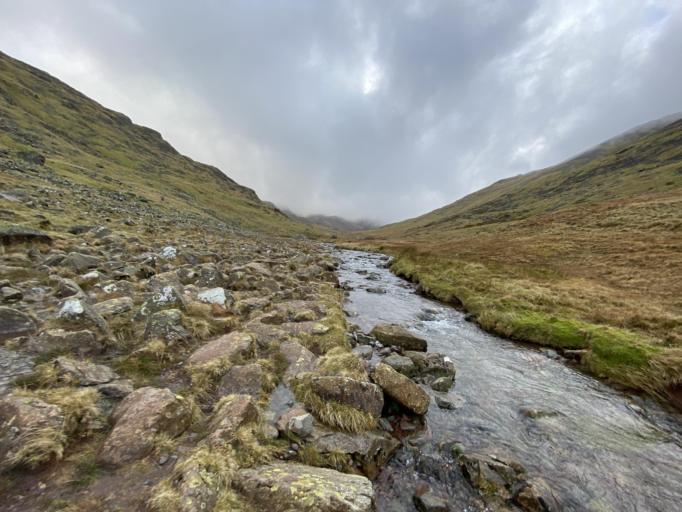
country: GB
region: England
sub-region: Cumbria
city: Keswick
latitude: 54.4827
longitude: -3.1996
